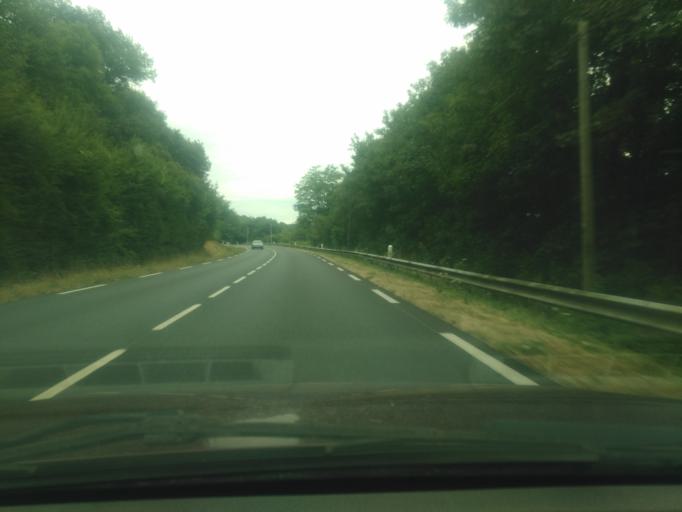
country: FR
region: Centre
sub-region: Departement de l'Indre
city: Saint-Gaultier
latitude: 46.6380
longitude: 1.3500
